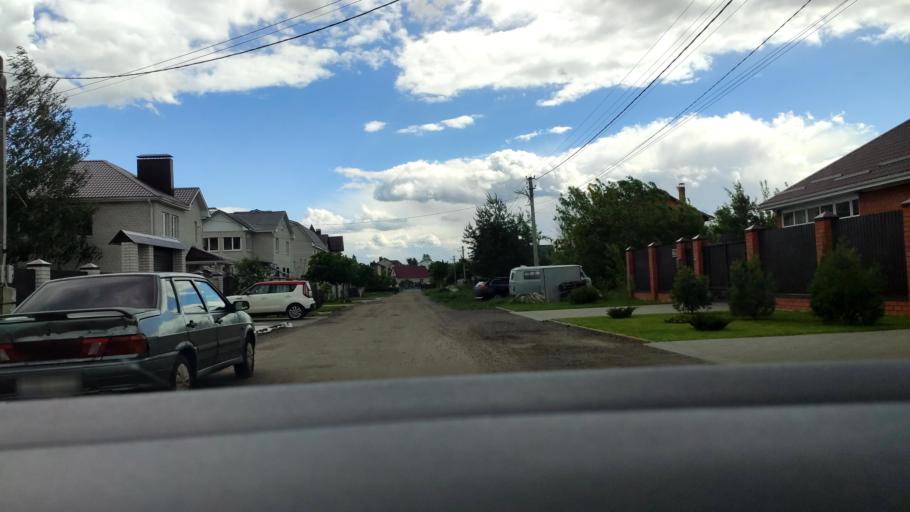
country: RU
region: Voronezj
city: Somovo
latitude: 51.6836
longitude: 39.3069
